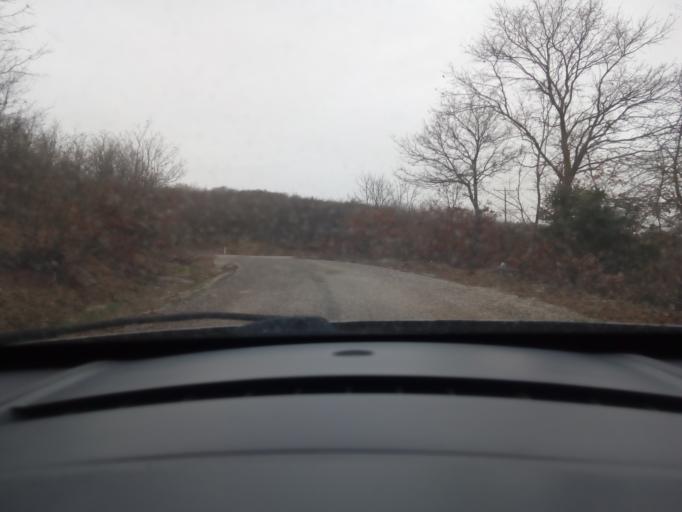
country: TR
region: Balikesir
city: Omerkoy
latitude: 39.8939
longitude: 28.0249
